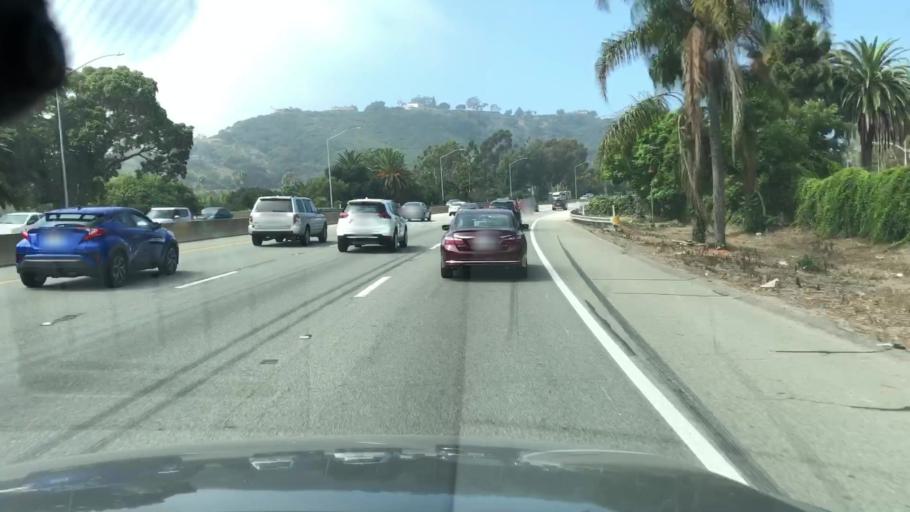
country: US
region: California
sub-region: Santa Barbara County
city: Santa Barbara
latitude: 34.4124
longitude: -119.6983
